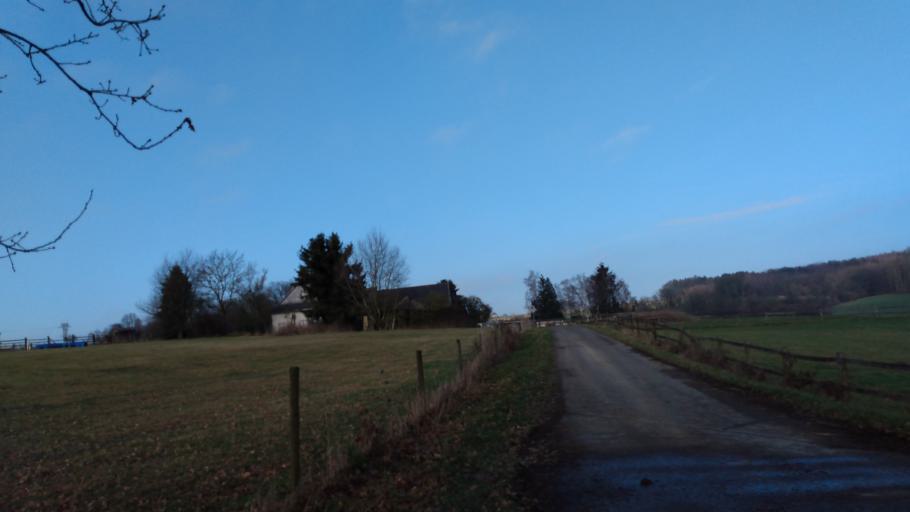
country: DE
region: Rheinland-Pfalz
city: Hirz-Maulsbach
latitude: 50.6796
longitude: 7.4617
